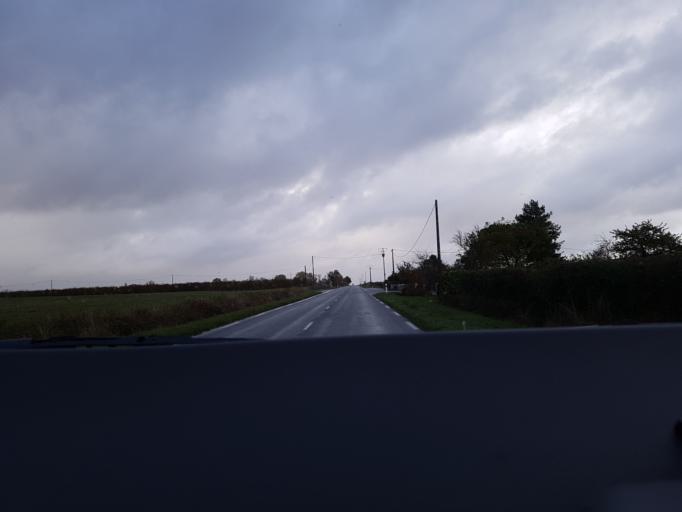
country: FR
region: Poitou-Charentes
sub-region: Departement des Deux-Sevres
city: Melle
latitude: 46.1859
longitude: -0.1814
